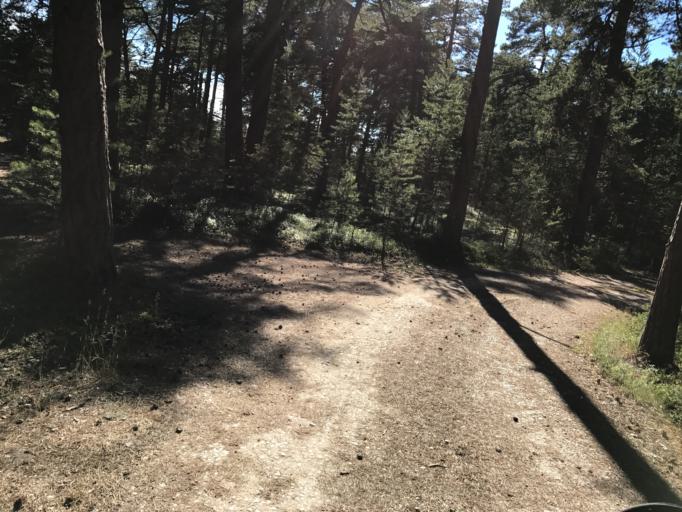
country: EE
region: Harju
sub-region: Paldiski linn
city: Paldiski
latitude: 59.3835
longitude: 24.2239
